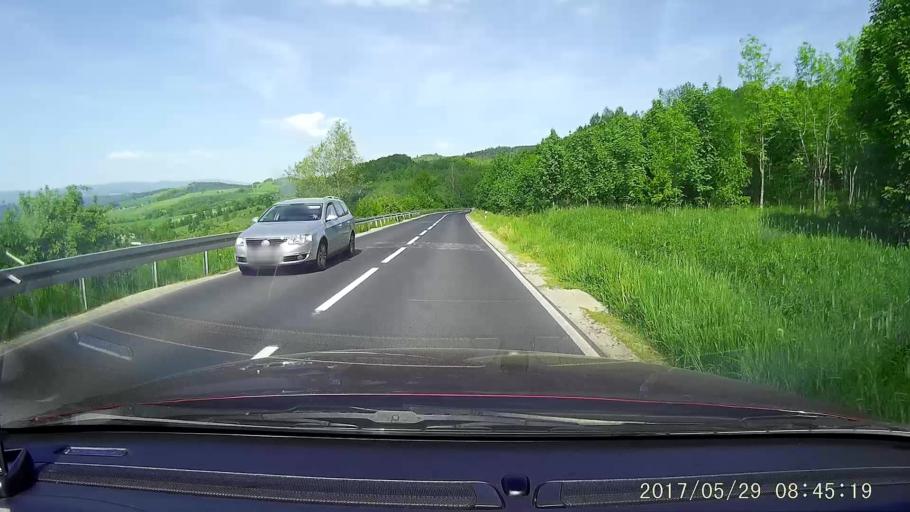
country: PL
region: Lower Silesian Voivodeship
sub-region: Powiat jeleniogorski
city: Jezow Sudecki
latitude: 50.9510
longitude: 15.8140
